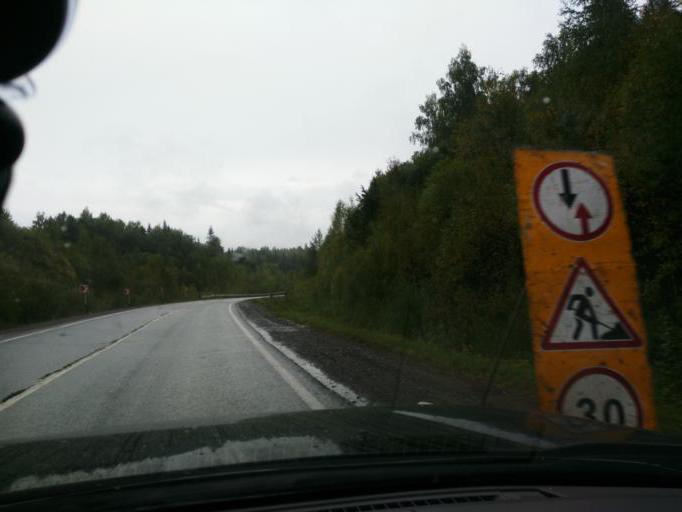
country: RU
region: Perm
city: Yugo-Kamskiy
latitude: 57.7475
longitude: 55.7117
